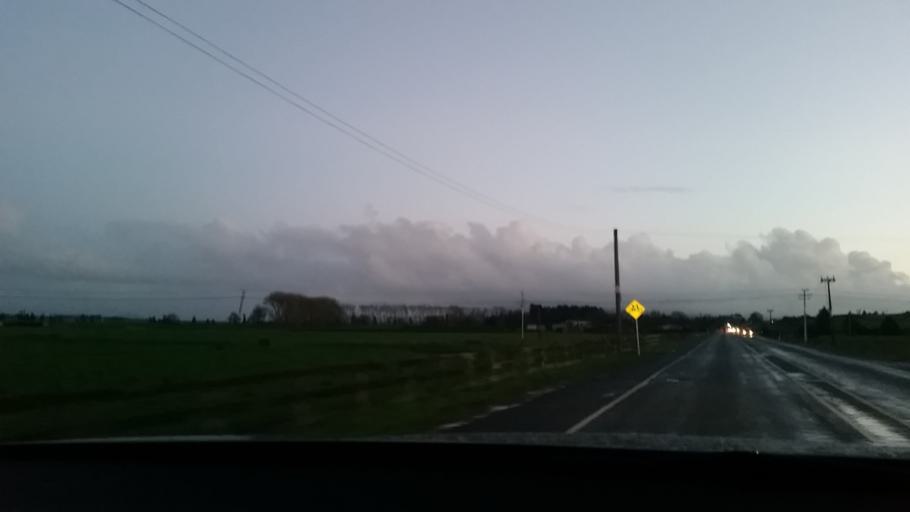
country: NZ
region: Waikato
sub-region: Hamilton City
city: Hamilton
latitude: -37.8067
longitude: 175.2402
